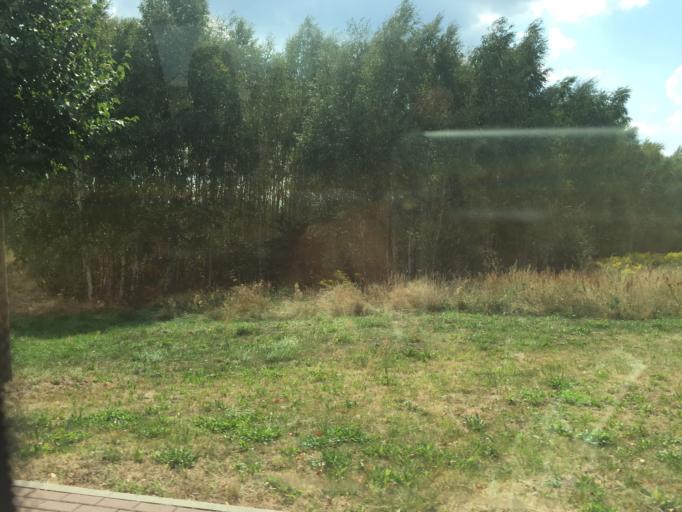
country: DE
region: Saxony
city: Schleife
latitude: 51.5109
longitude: 14.4939
